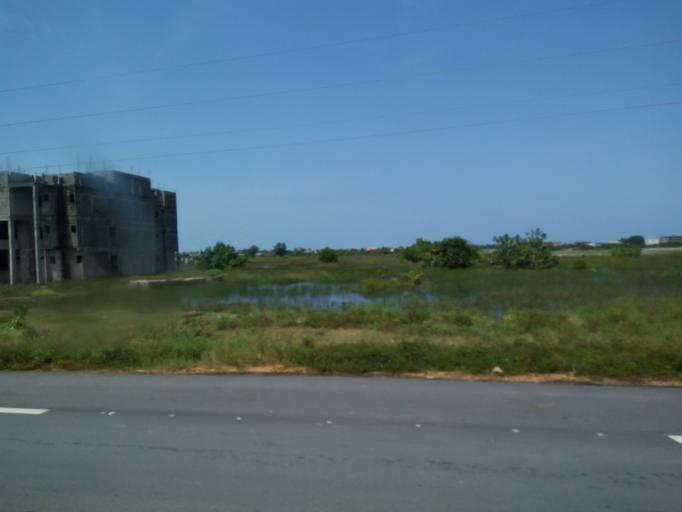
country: CI
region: Sud-Comoe
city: Grand-Bassam
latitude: 5.2282
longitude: -3.7462
